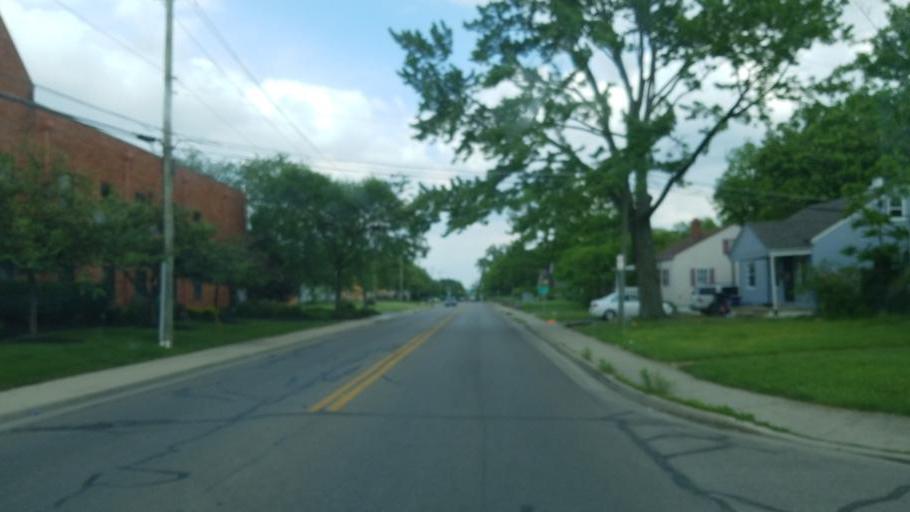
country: US
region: Ohio
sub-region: Franklin County
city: Minerva Park
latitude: 40.0271
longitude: -82.9563
